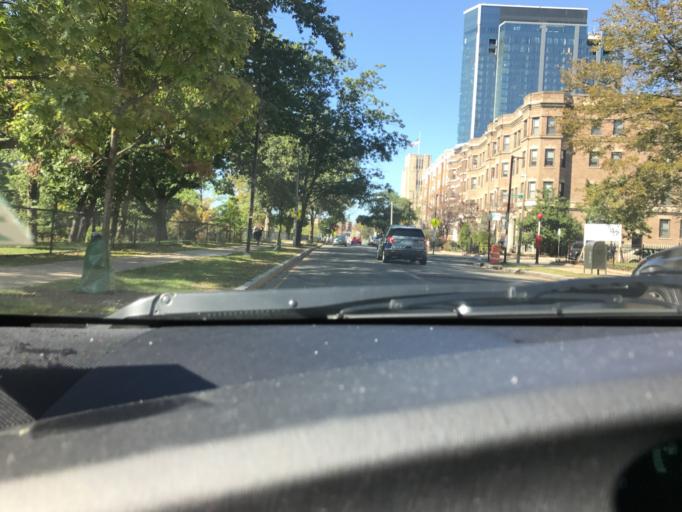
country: US
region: Massachusetts
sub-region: Norfolk County
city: Brookline
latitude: 42.3414
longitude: -71.1007
